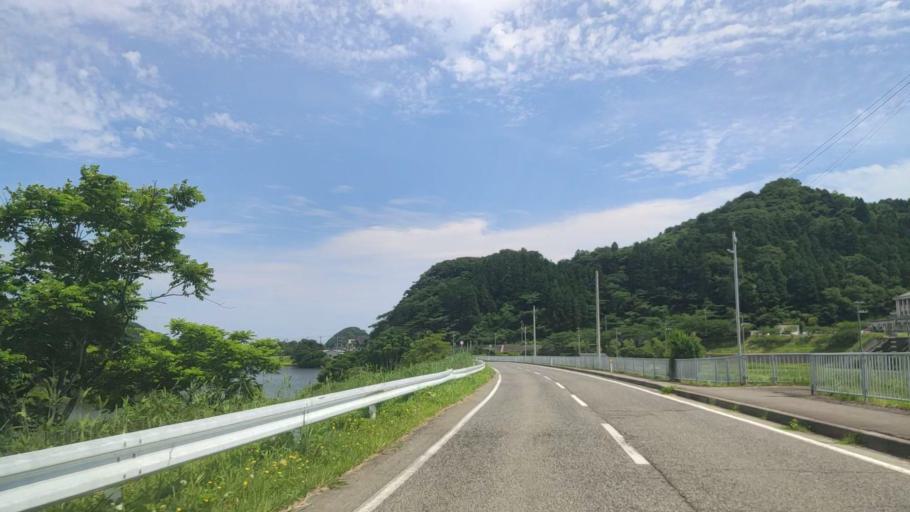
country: JP
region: Hyogo
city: Toyooka
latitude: 35.6495
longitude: 134.7638
